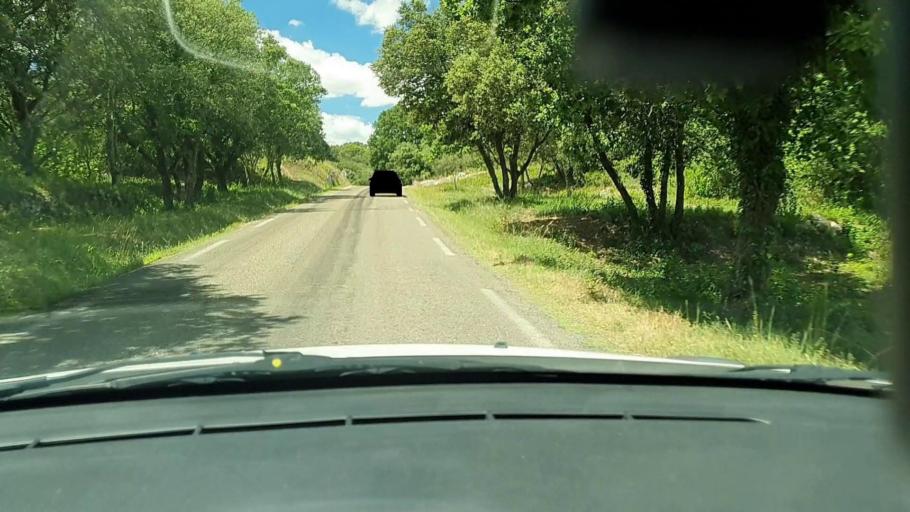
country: FR
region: Languedoc-Roussillon
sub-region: Departement du Gard
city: Cabrieres
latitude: 43.9548
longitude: 4.4504
